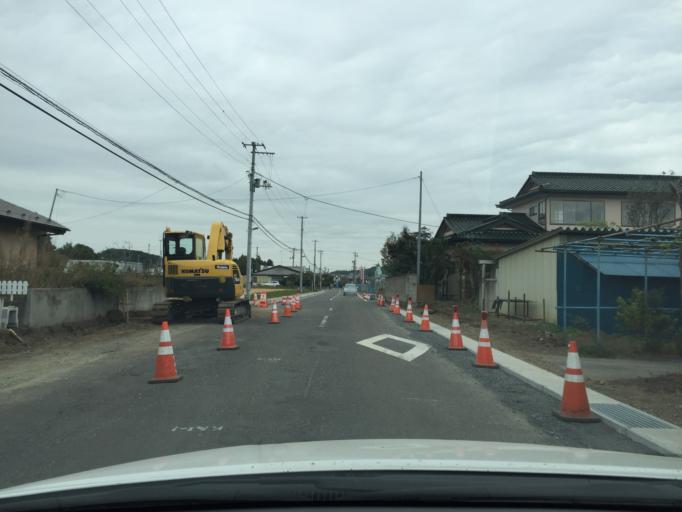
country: JP
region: Tochigi
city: Kuroiso
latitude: 37.1383
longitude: 140.1515
